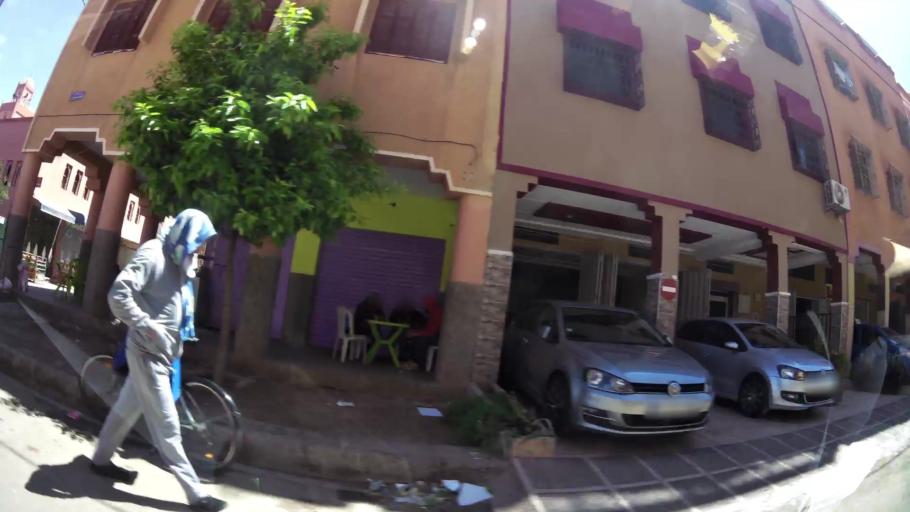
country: MA
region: Marrakech-Tensift-Al Haouz
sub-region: Marrakech
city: Marrakesh
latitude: 31.6368
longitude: -8.0597
